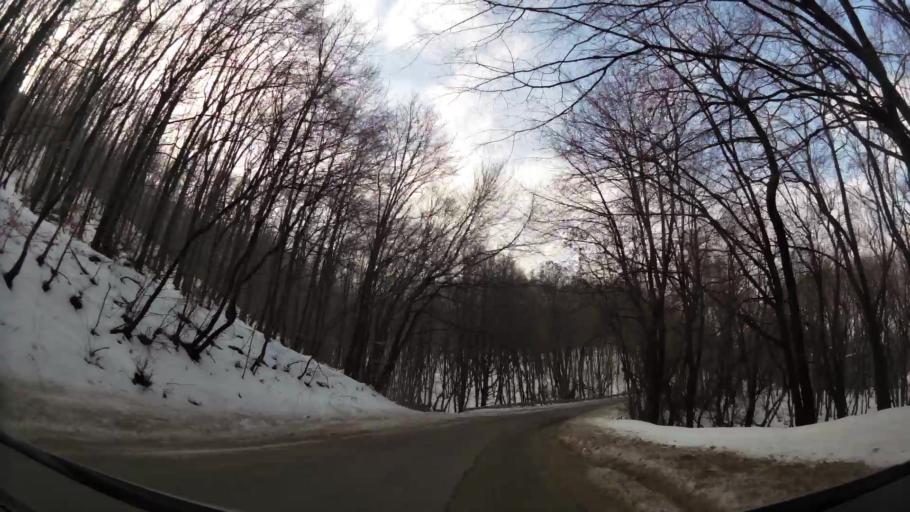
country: BG
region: Sofia-Capital
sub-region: Stolichna Obshtina
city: Sofia
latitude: 42.6448
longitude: 23.2408
